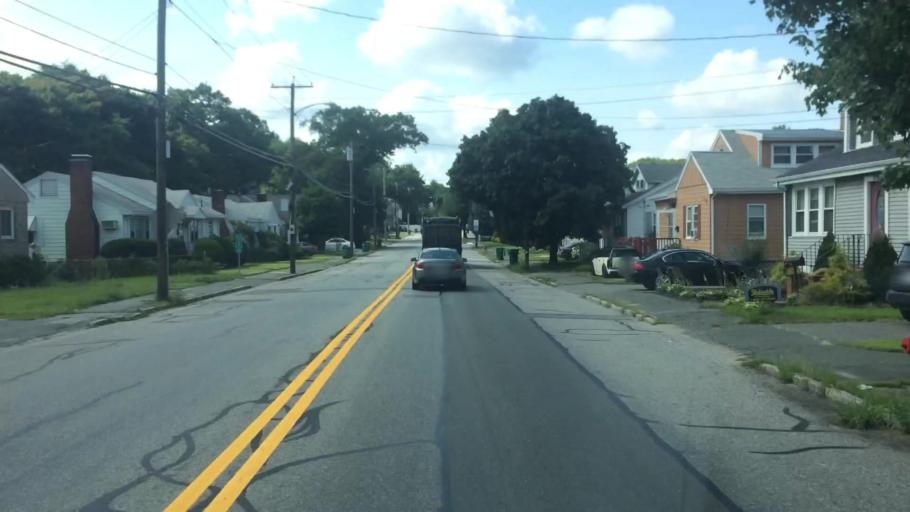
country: US
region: Massachusetts
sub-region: Essex County
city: South Peabody
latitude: 42.4980
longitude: -70.9713
